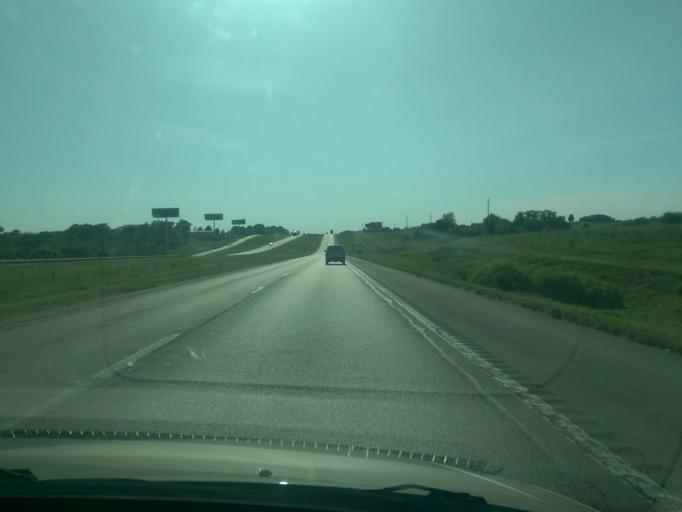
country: US
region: Missouri
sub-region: Lafayette County
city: Odessa
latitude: 39.0098
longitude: -94.0082
